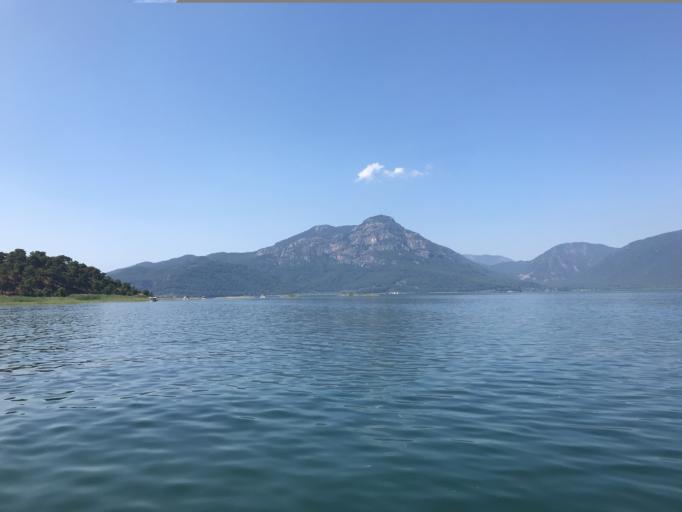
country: TR
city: Dalyan
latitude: 36.9002
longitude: 28.6449
